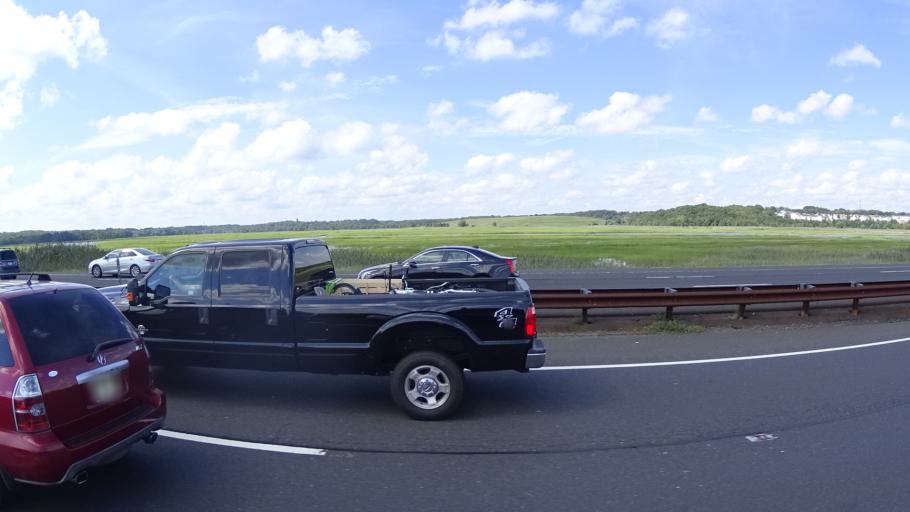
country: US
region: New Jersey
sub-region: Middlesex County
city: Laurence Harbor
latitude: 40.4499
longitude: -74.2702
